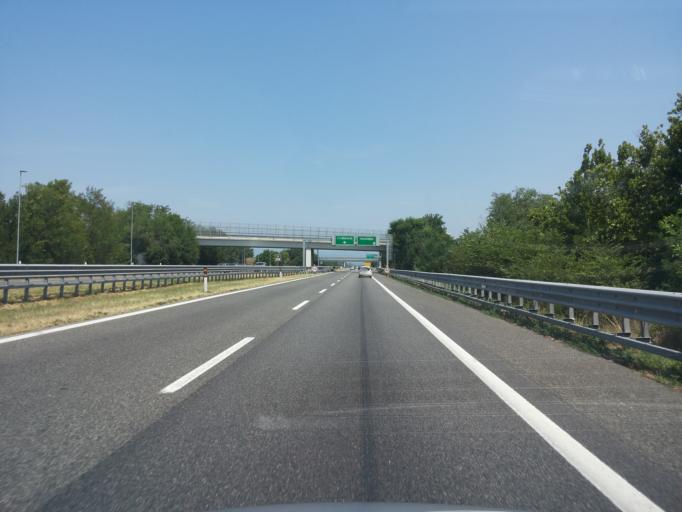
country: IT
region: Lombardy
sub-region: Provincia di Brescia
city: Manerbio
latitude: 45.3618
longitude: 10.1680
